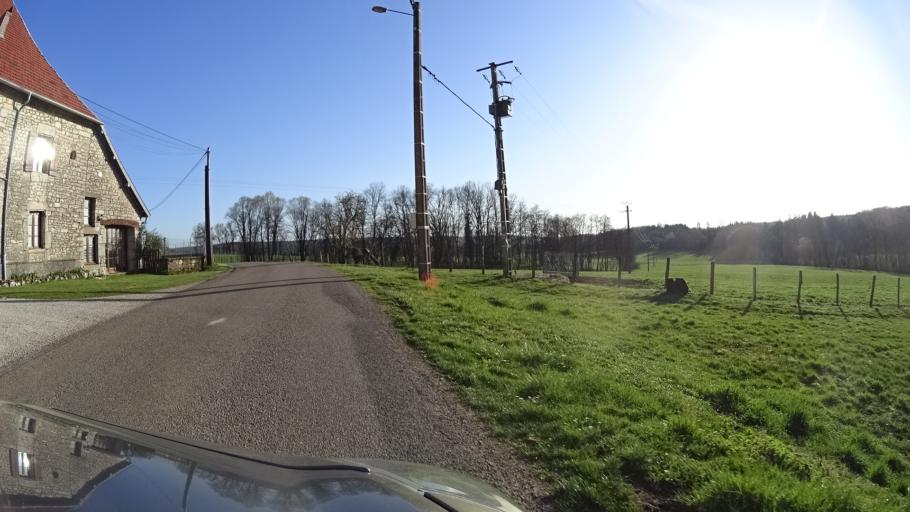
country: FR
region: Franche-Comte
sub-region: Departement du Doubs
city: Morre
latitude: 47.1983
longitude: 6.0506
